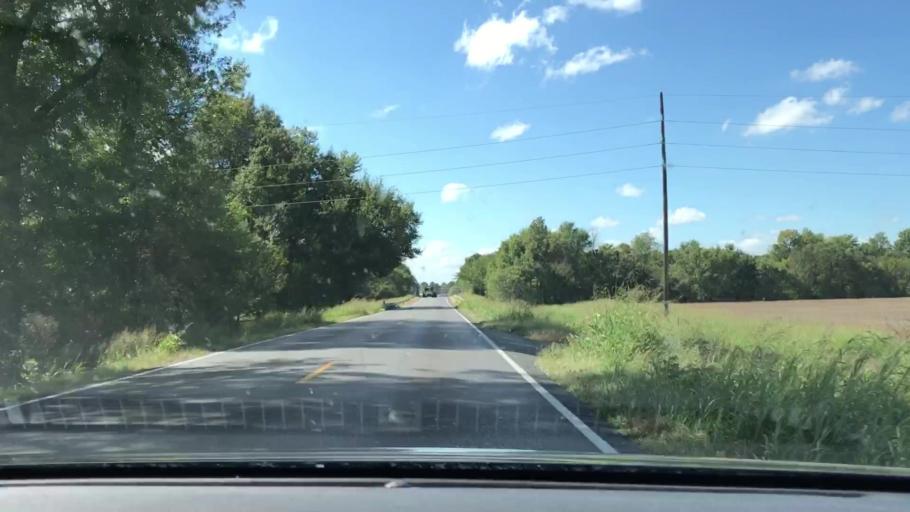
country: US
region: Kentucky
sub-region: Graves County
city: Mayfield
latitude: 36.7499
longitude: -88.6157
